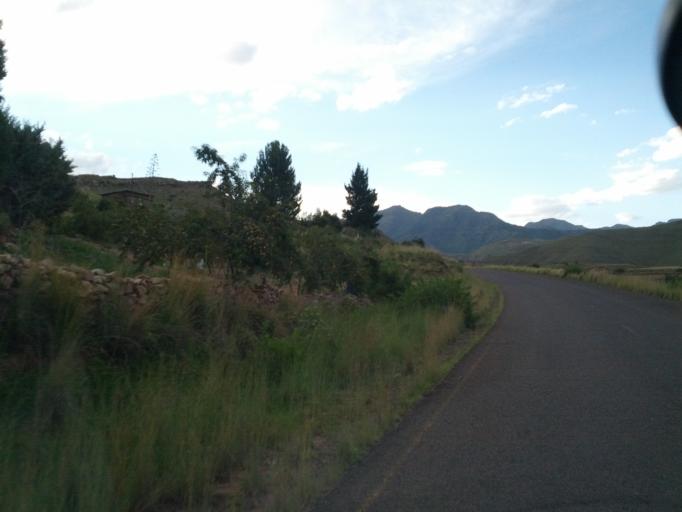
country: LS
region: Qacha's Nek
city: Qacha's Nek
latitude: -30.0671
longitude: 28.5330
